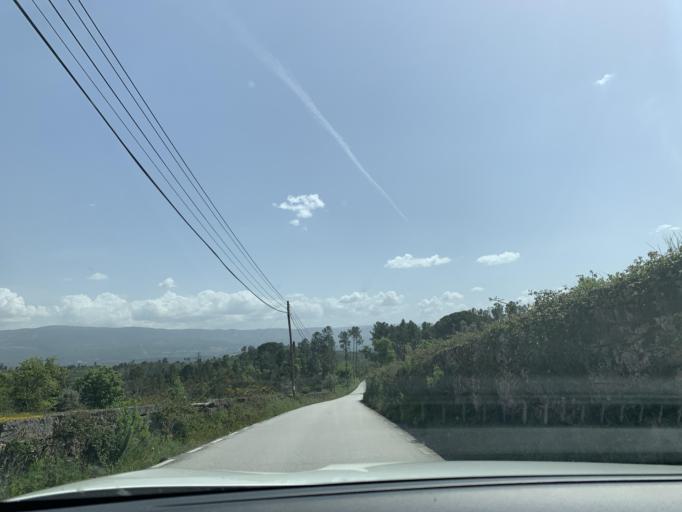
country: PT
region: Guarda
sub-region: Fornos de Algodres
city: Fornos de Algodres
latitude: 40.5863
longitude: -7.6348
